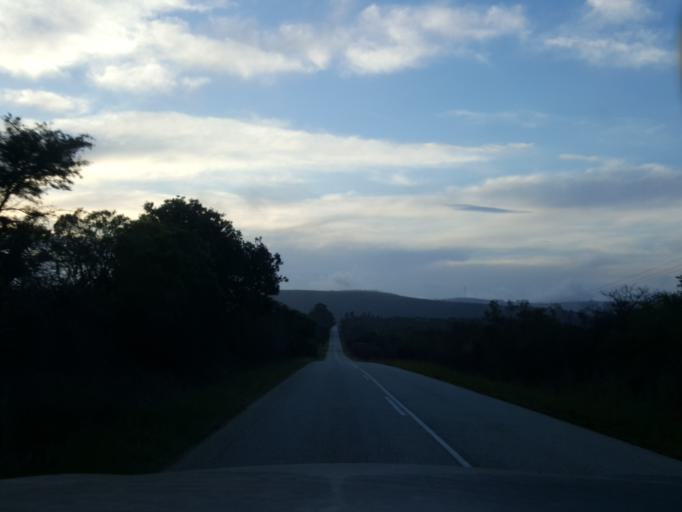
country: ZA
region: Eastern Cape
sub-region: Cacadu District Municipality
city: Grahamstown
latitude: -33.3897
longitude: 26.4741
